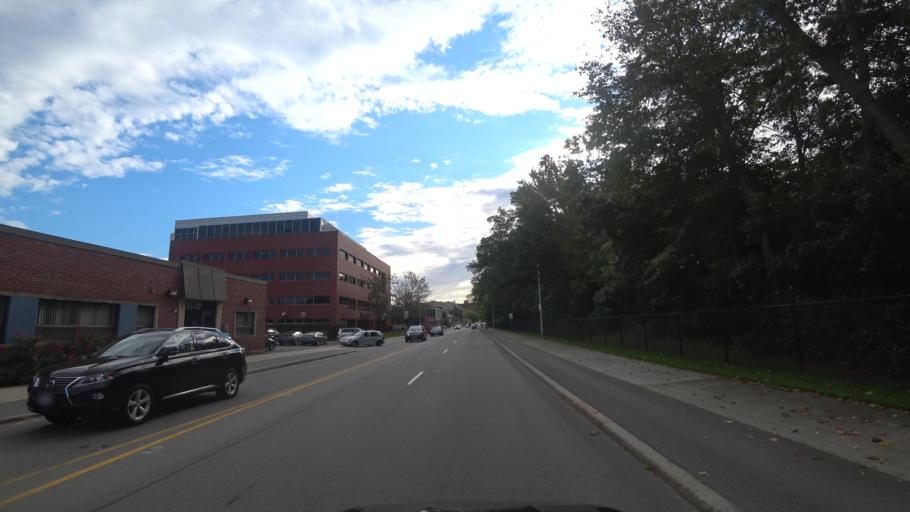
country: US
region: Massachusetts
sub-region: Middlesex County
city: Arlington
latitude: 42.3905
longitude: -71.1537
